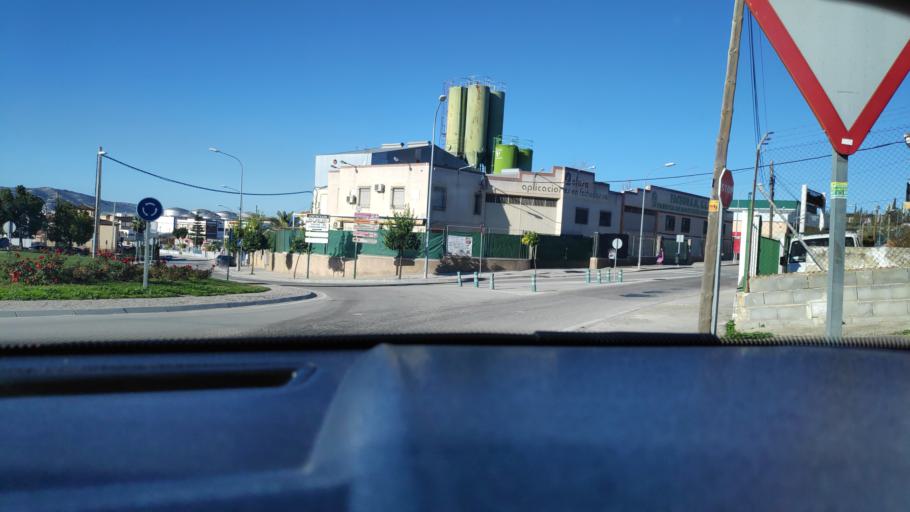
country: ES
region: Andalusia
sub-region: Province of Cordoba
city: Baena
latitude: 37.6231
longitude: -4.3080
